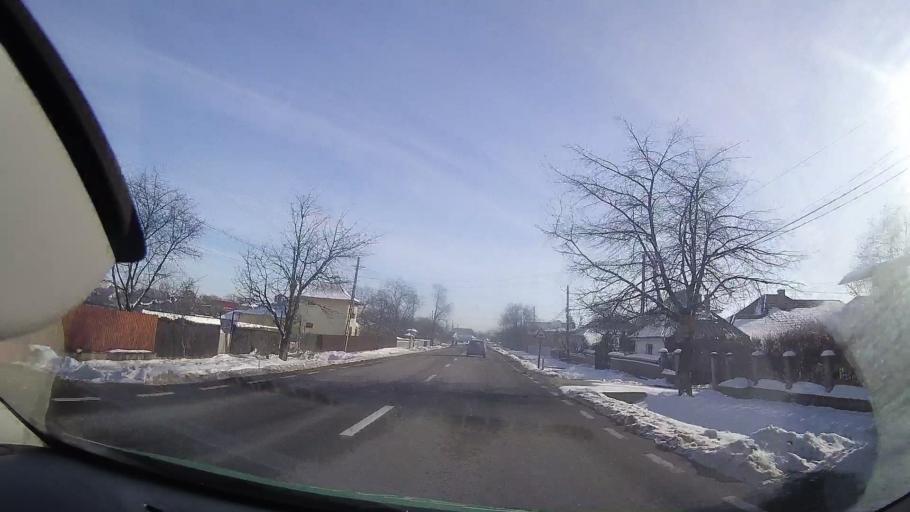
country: RO
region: Neamt
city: Bodesti
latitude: 47.0537
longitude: 26.3987
